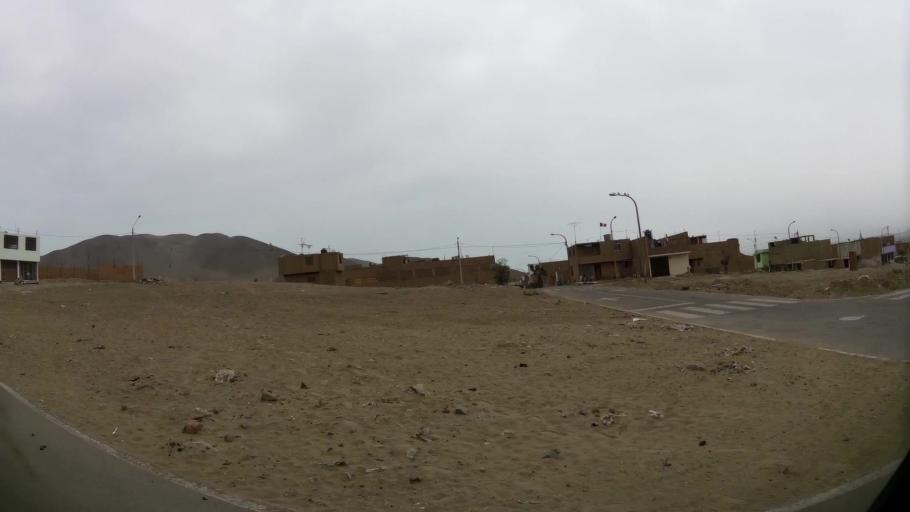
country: PE
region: Lima
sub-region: Lima
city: Santa Rosa
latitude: -11.7914
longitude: -77.1556
